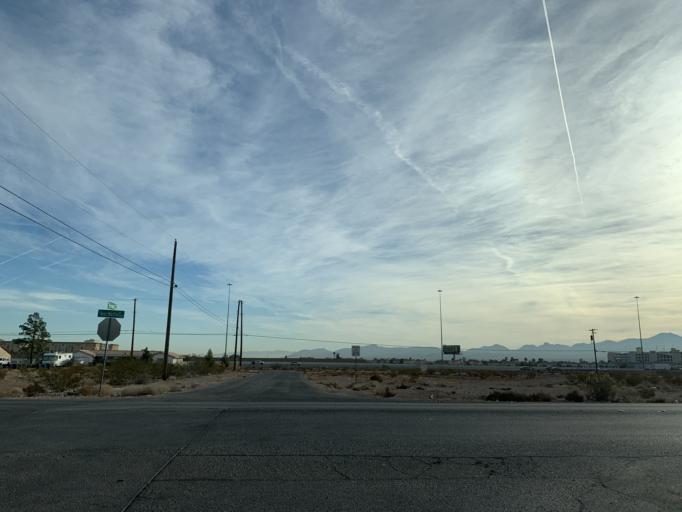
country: US
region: Nevada
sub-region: Clark County
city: Enterprise
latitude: 36.0172
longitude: -115.1834
